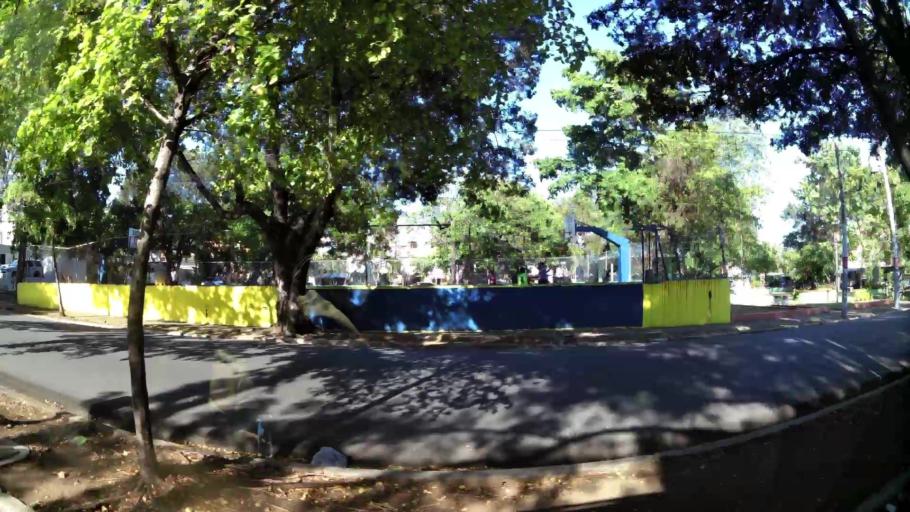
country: DO
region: Nacional
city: Bella Vista
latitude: 18.4492
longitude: -69.9355
